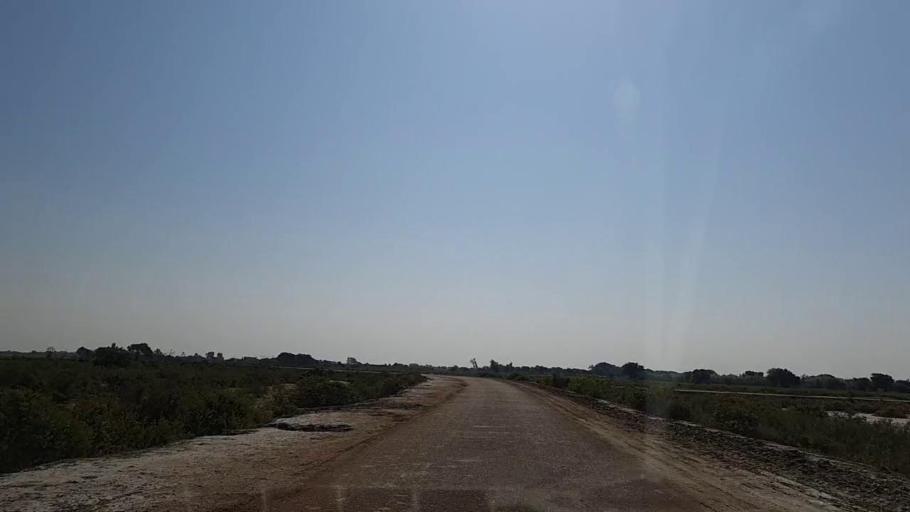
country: PK
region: Sindh
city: Chuhar Jamali
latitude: 24.5270
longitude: 68.0842
